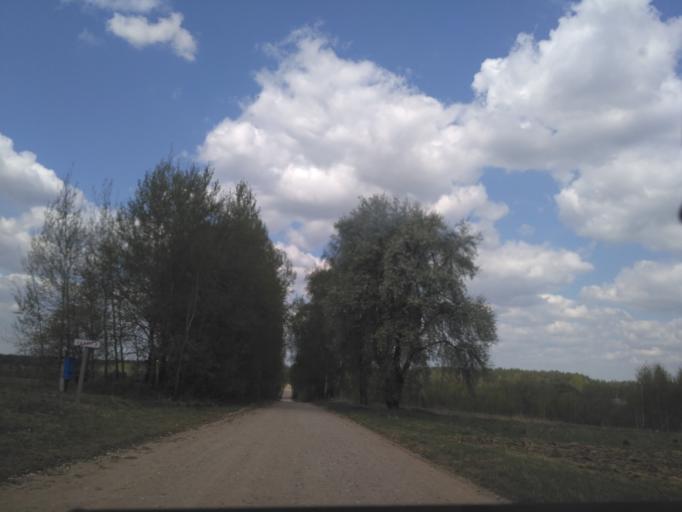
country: BY
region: Minsk
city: Il'ya
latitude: 54.2785
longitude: 27.3058
